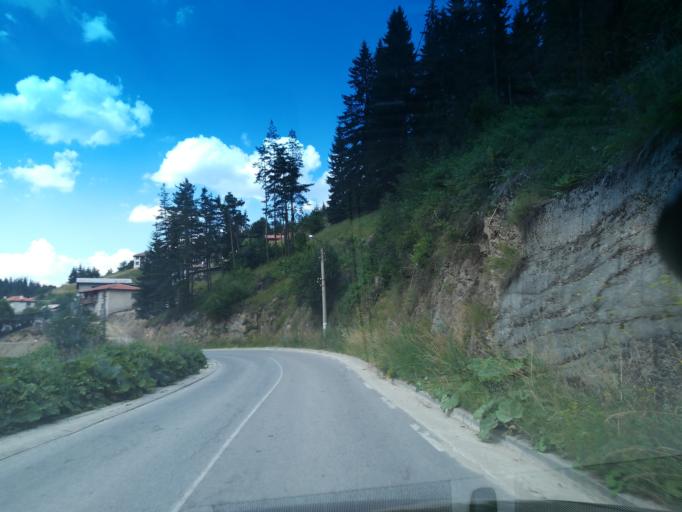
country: BG
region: Smolyan
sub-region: Obshtina Smolyan
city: Smolyan
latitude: 41.6544
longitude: 24.6358
